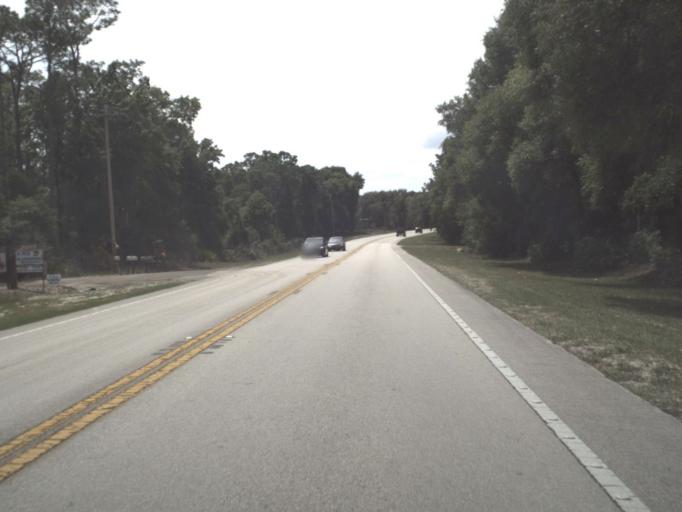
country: US
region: Florida
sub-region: Lake County
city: Lake Mack-Forest Hills
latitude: 28.9024
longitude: -81.4558
